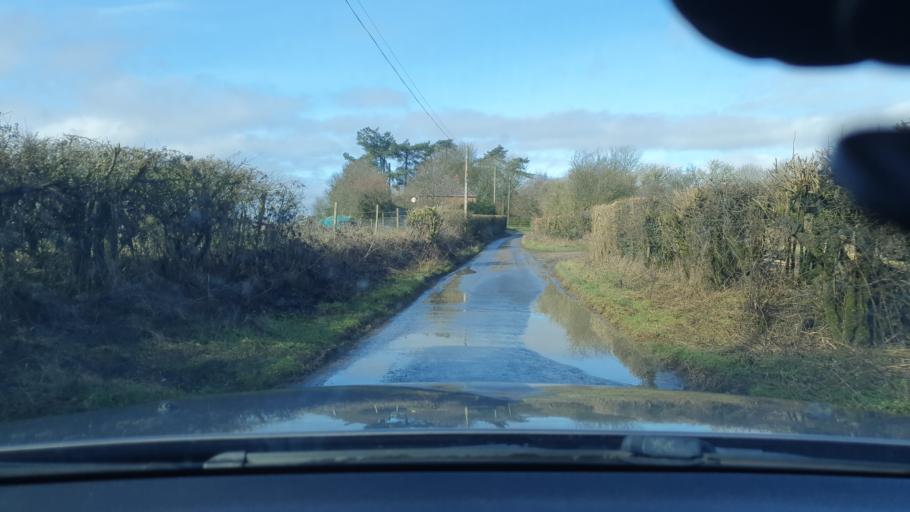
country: GB
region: England
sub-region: Wiltshire
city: Shalbourne
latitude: 51.3498
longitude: -1.5135
